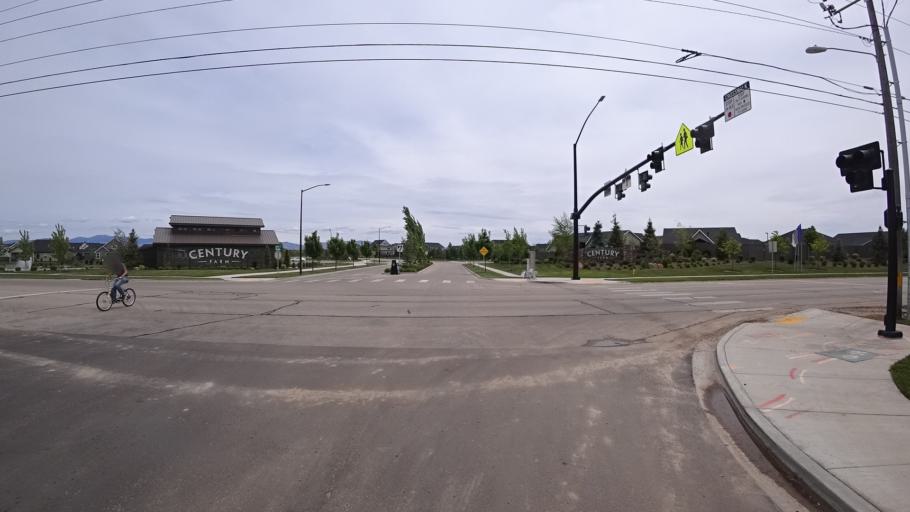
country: US
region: Idaho
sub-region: Ada County
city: Meridian
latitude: 43.5534
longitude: -116.3545
